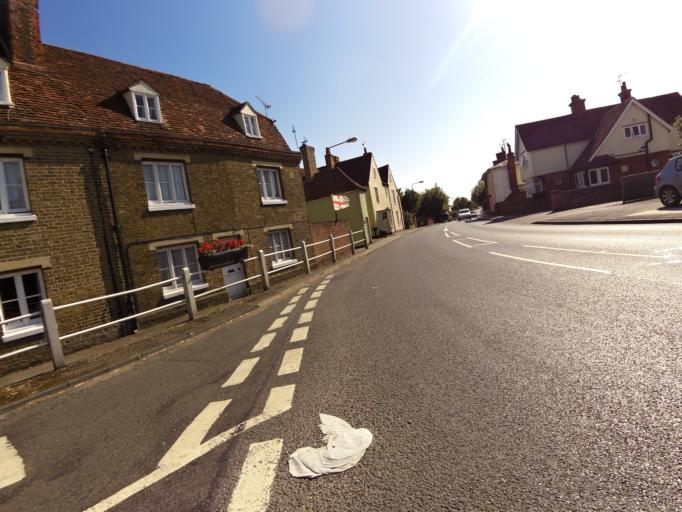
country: GB
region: England
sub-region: Essex
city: Kelvedon
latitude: 51.8329
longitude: 0.6973
